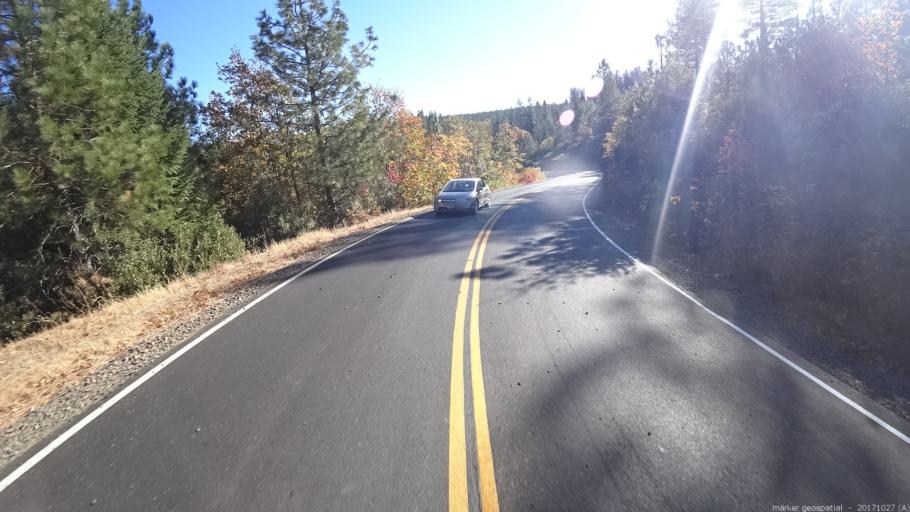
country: US
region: California
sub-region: Shasta County
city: Burney
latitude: 40.8683
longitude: -121.9039
